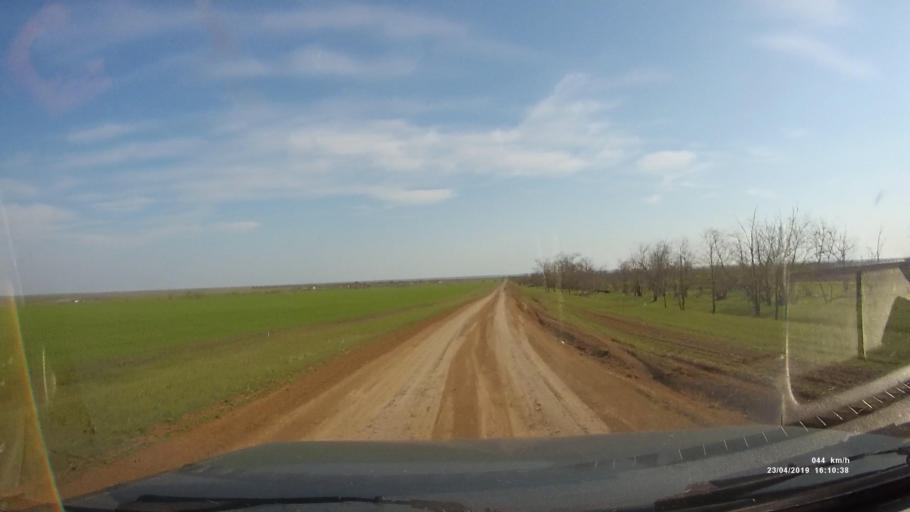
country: RU
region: Rostov
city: Remontnoye
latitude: 46.4806
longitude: 43.1230
